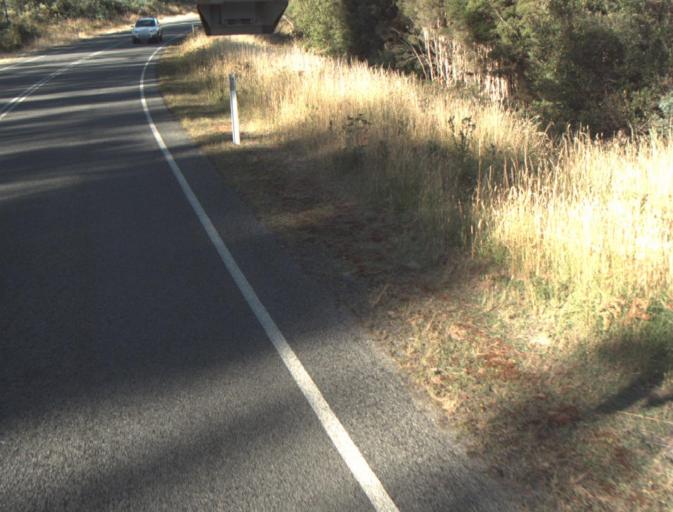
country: AU
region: Tasmania
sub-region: Launceston
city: Newstead
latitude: -41.4268
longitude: 147.2548
